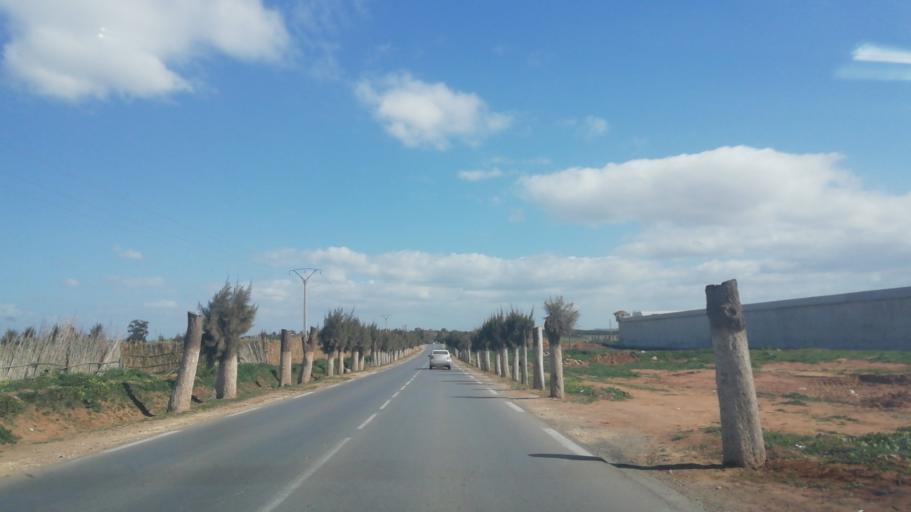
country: DZ
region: Mostaganem
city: Mostaganem
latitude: 35.9995
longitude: 0.3093
